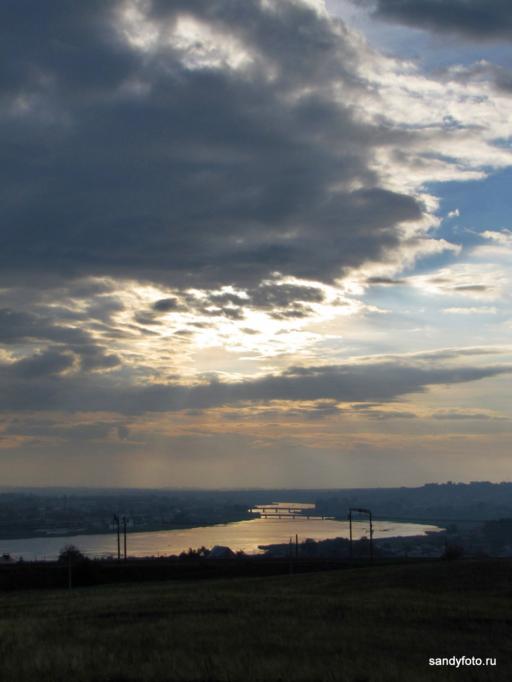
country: RU
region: Chelyabinsk
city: Troitsk
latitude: 54.0857
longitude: 61.6031
